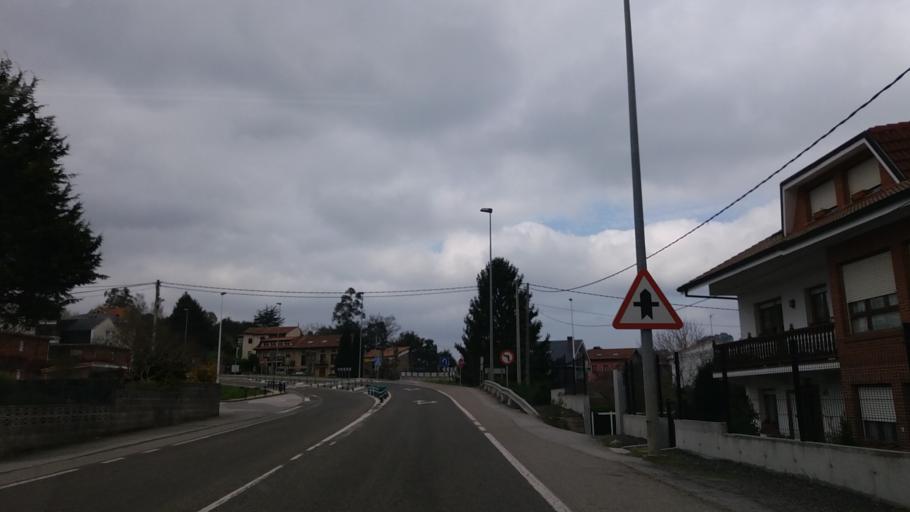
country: ES
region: Cantabria
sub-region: Provincia de Cantabria
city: Reocin
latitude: 43.3558
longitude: -4.1130
